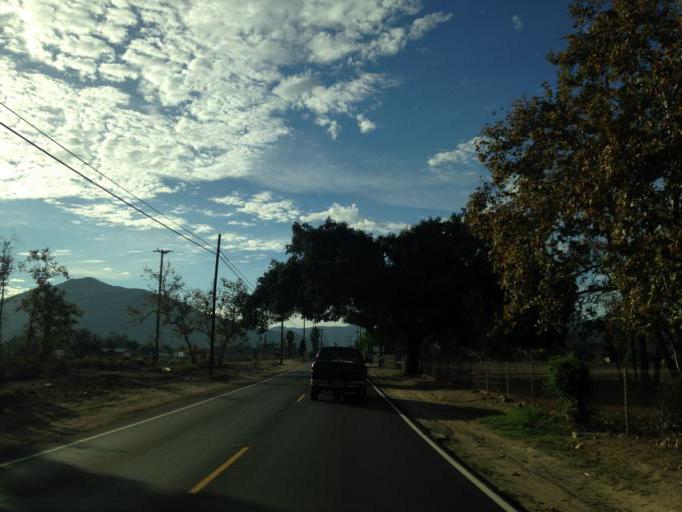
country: US
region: California
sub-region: San Diego County
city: Rainbow
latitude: 33.3734
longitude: -117.0790
